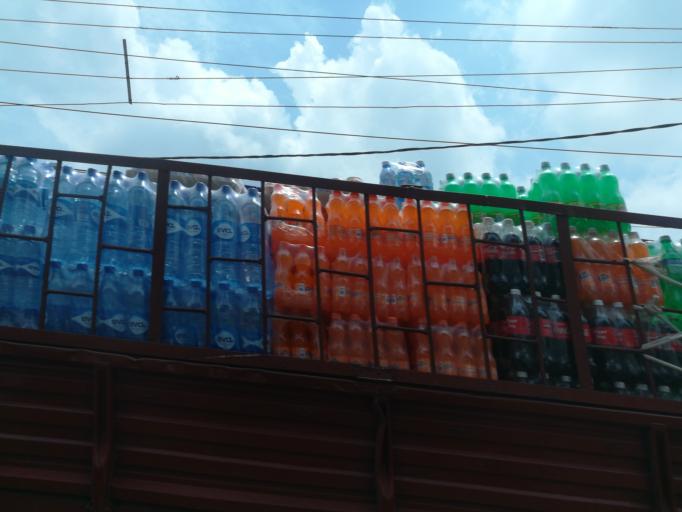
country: NG
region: Lagos
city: Ikeja
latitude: 6.5924
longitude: 3.3587
